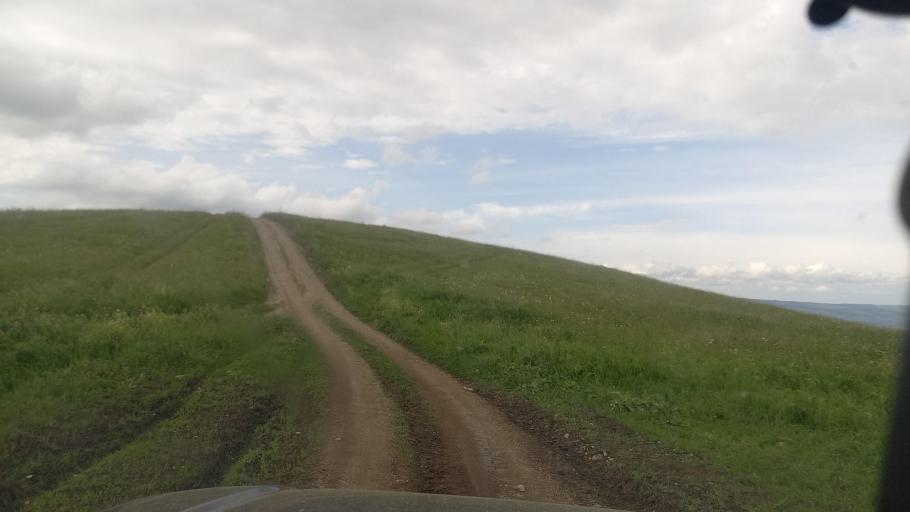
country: RU
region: Krasnodarskiy
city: Peredovaya
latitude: 44.0601
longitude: 41.3632
